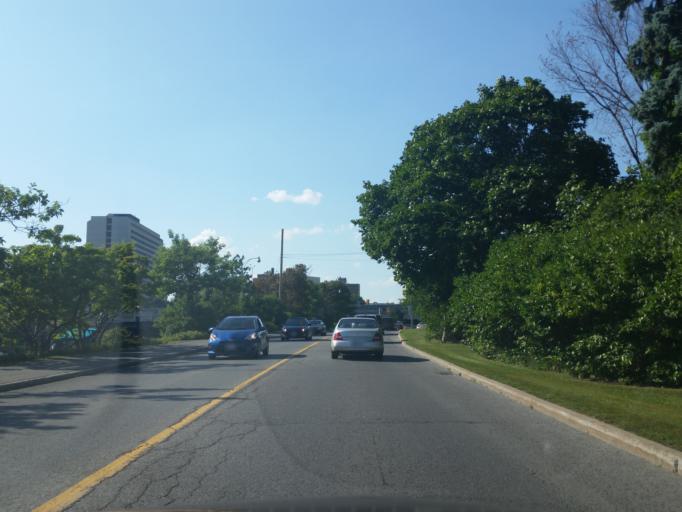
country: CA
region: Ontario
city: Ottawa
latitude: 45.4104
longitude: -75.6818
